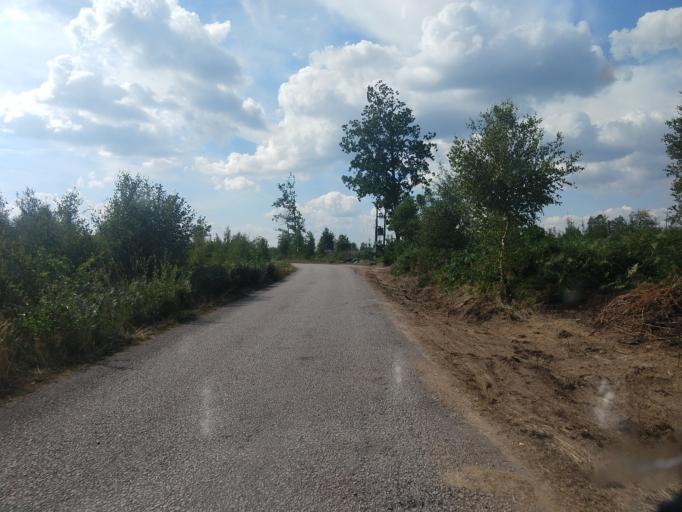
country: SE
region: Blekinge
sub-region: Karlskrona Kommun
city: Rodeby
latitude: 56.2448
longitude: 15.5552
